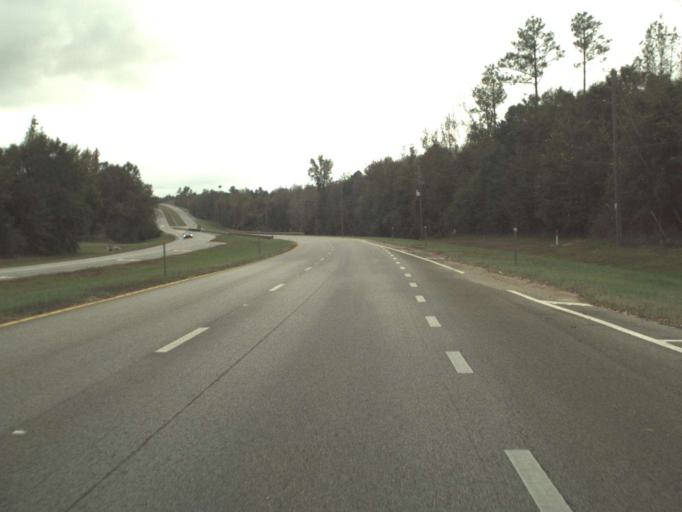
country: US
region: Florida
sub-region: Escambia County
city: Molino
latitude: 30.7789
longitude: -87.3380
